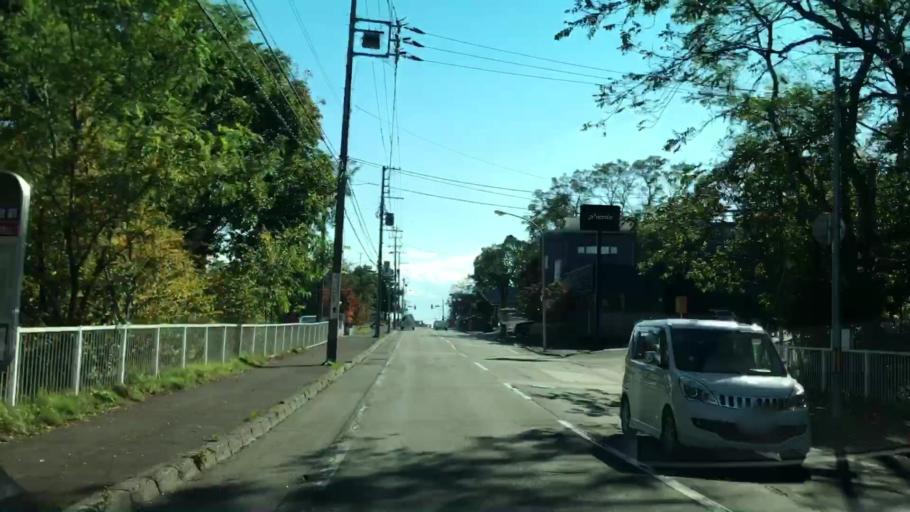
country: JP
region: Hokkaido
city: Sapporo
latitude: 43.0377
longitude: 141.3242
